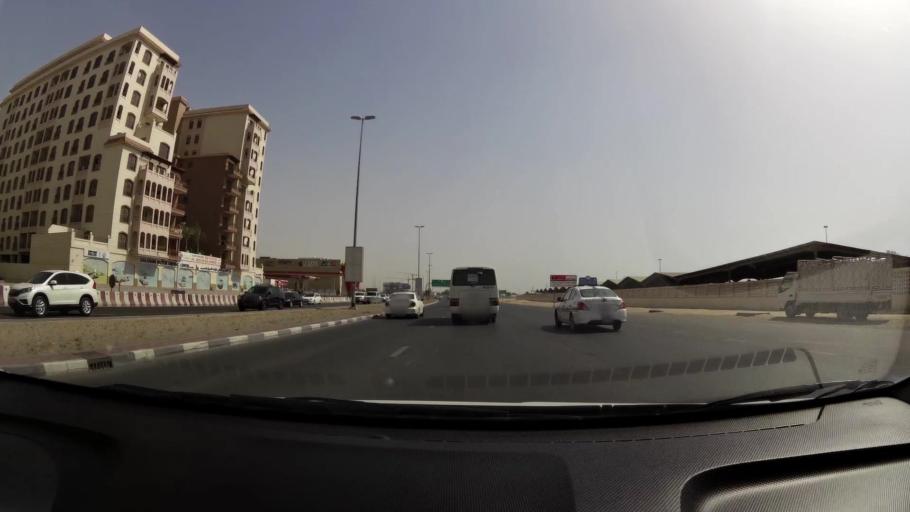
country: AE
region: Ash Shariqah
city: Sharjah
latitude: 25.2855
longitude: 55.3987
